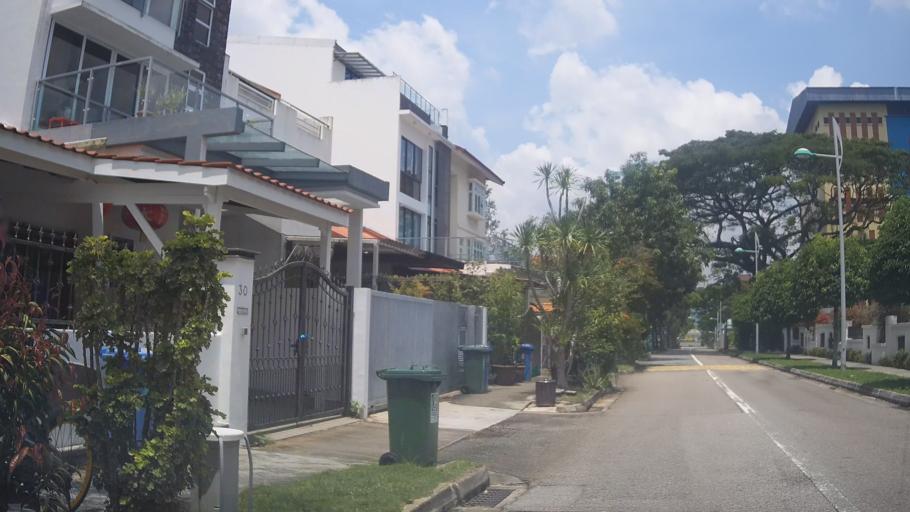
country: SG
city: Singapore
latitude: 1.3419
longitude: 103.7732
